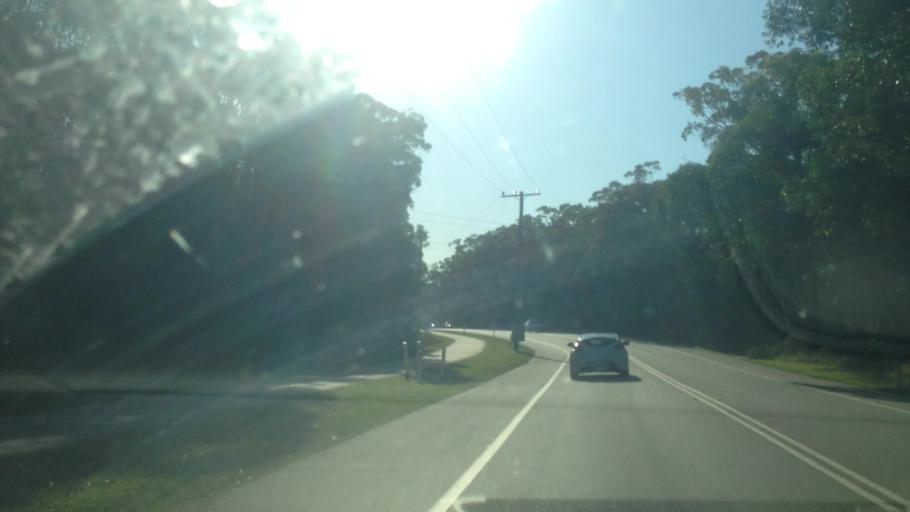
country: AU
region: New South Wales
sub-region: Lake Macquarie Shire
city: Dora Creek
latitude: -33.1091
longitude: 151.5015
